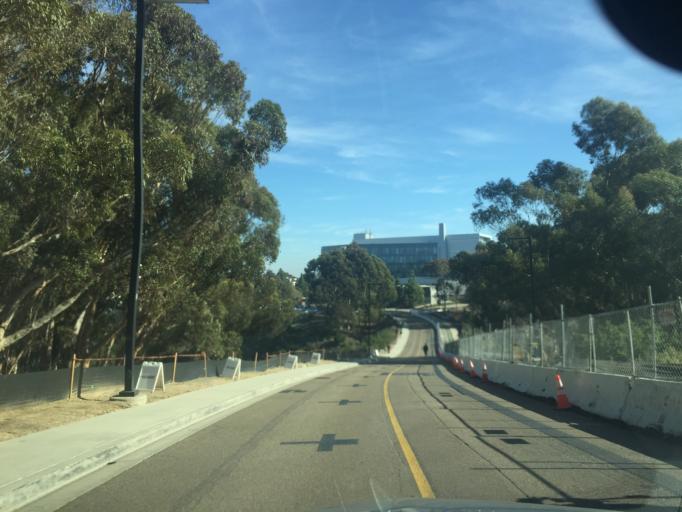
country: US
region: California
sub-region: San Diego County
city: La Jolla
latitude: 32.8834
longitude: -117.2379
